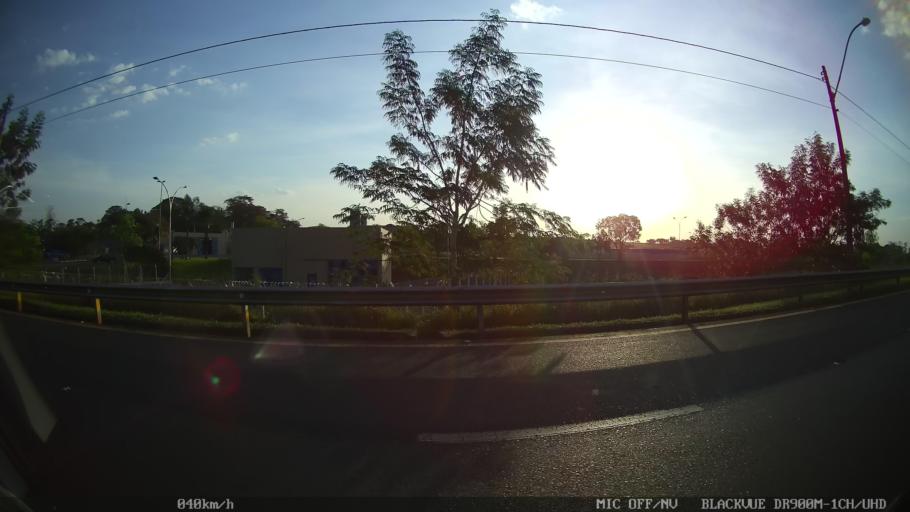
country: BR
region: Sao Paulo
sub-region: Ribeirao Preto
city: Ribeirao Preto
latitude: -21.1050
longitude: -47.8107
